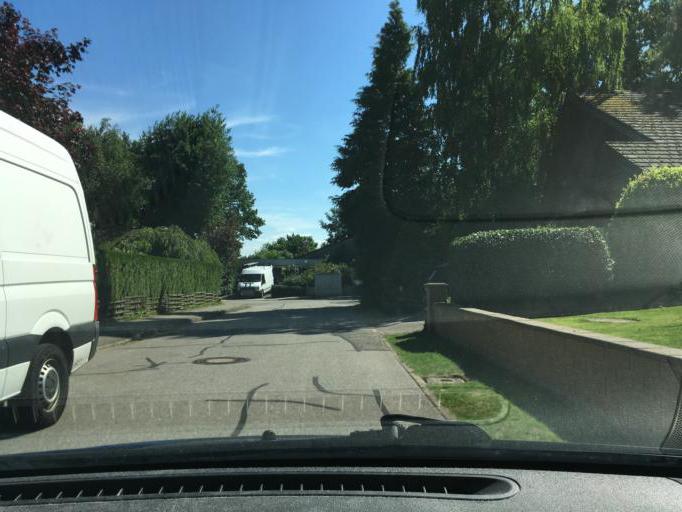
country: DE
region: Lower Saxony
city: Buchholz in der Nordheide
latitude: 53.3803
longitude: 9.8858
